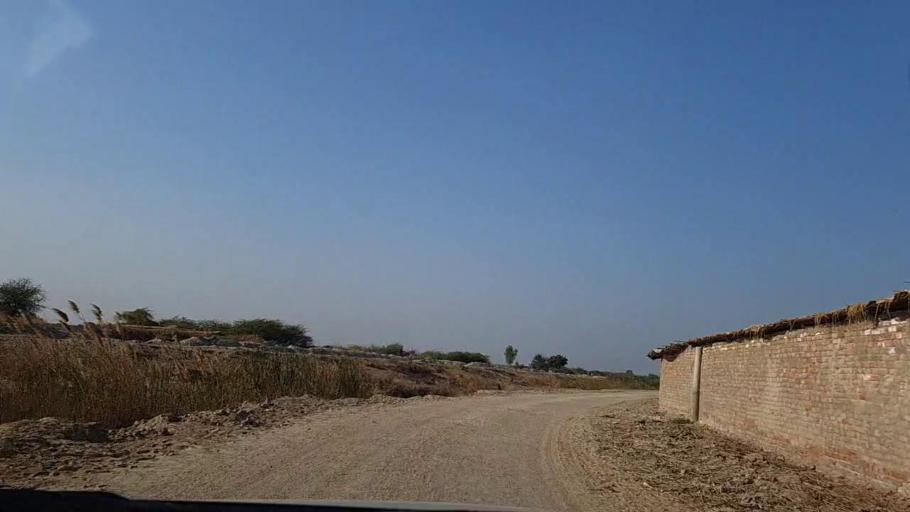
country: PK
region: Sindh
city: Mirwah Gorchani
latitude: 25.2307
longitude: 68.9815
